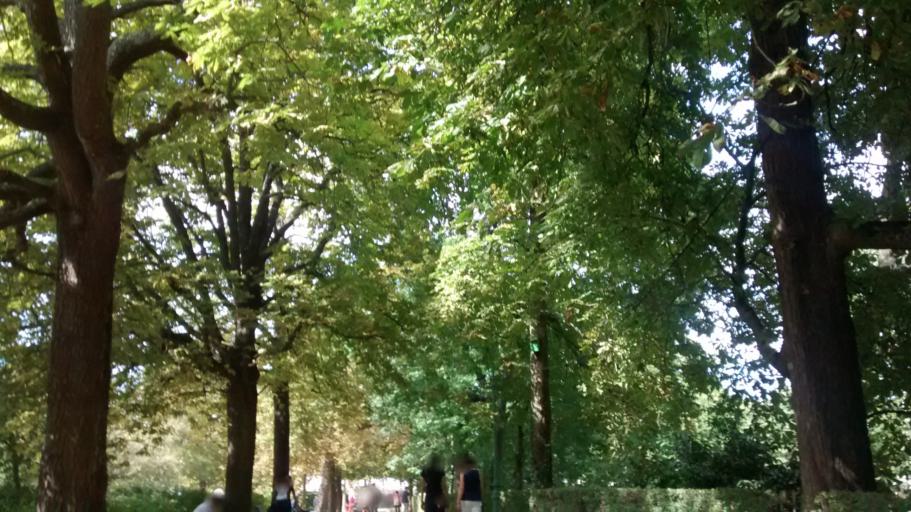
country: FR
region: Brittany
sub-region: Departement d'Ille-et-Vilaine
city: Rennes
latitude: 48.1146
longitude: -1.6713
